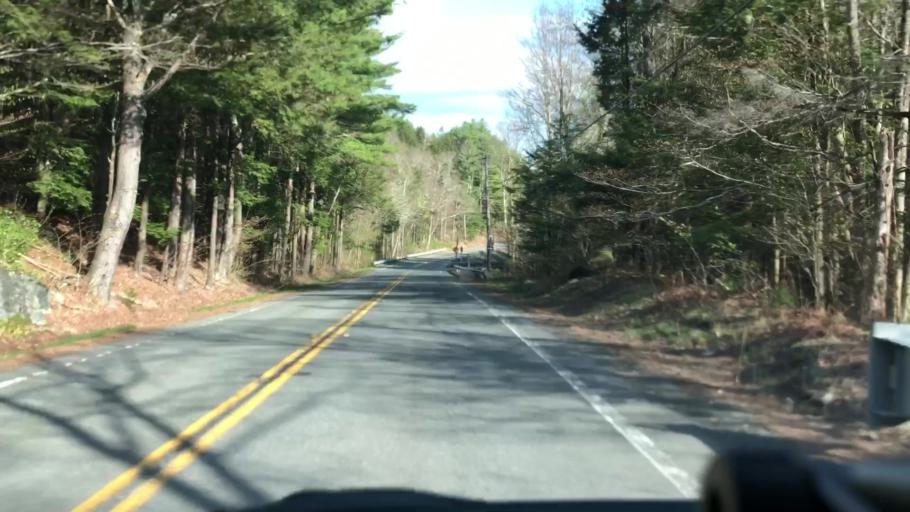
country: US
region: Massachusetts
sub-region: Hampshire County
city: Chesterfield
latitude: 42.3511
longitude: -72.9036
